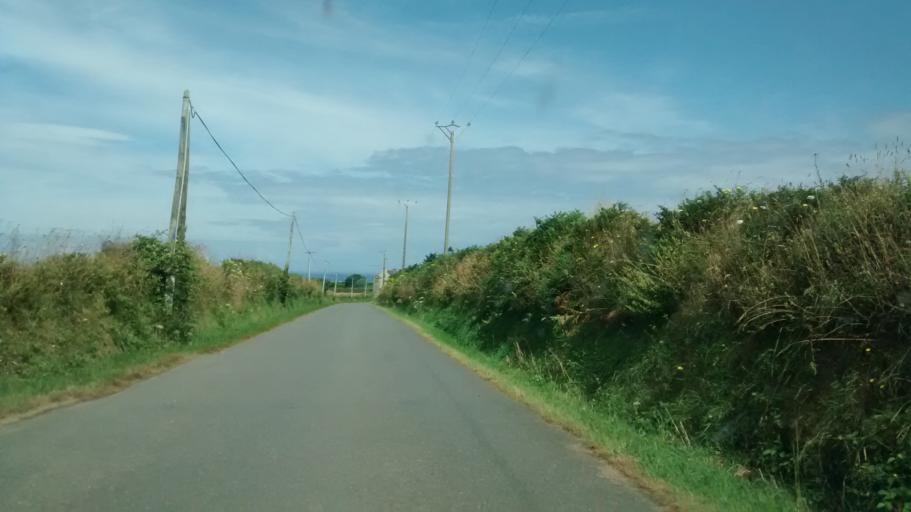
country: FR
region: Brittany
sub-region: Departement du Finistere
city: Plouguerneau
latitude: 48.6130
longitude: -4.4794
